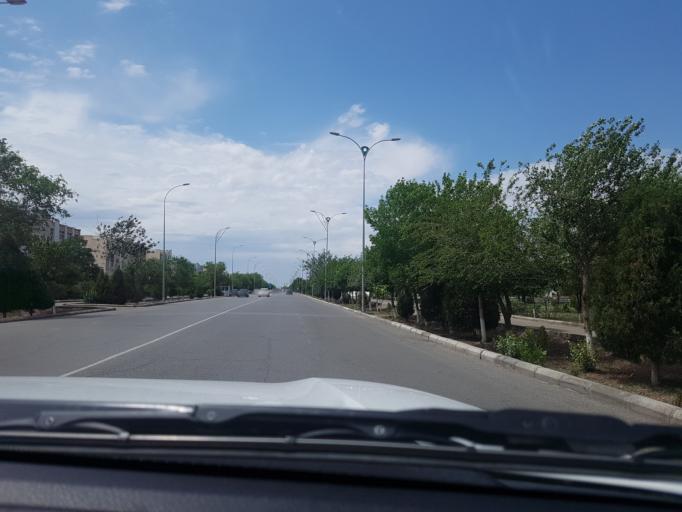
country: TM
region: Dasoguz
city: Dasoguz
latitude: 41.8417
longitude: 59.9399
